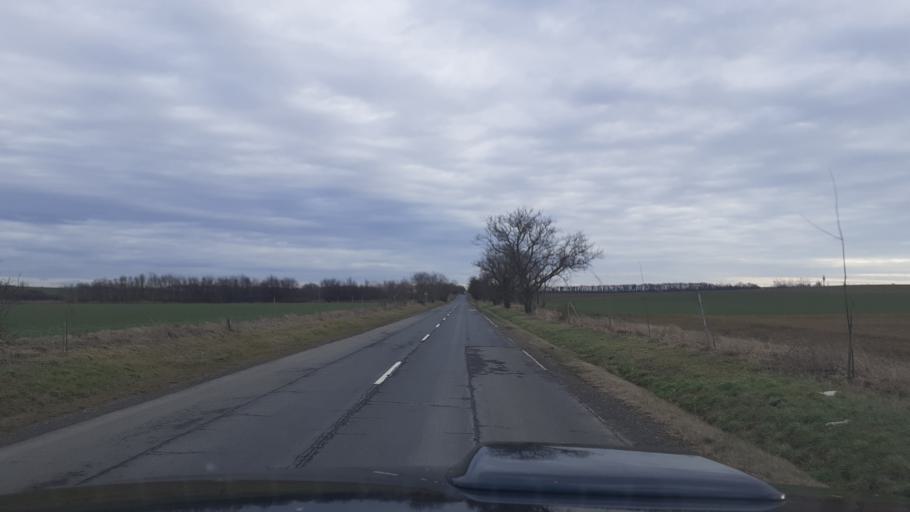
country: HU
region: Fejer
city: Mezofalva
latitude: 46.9844
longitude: 18.7121
